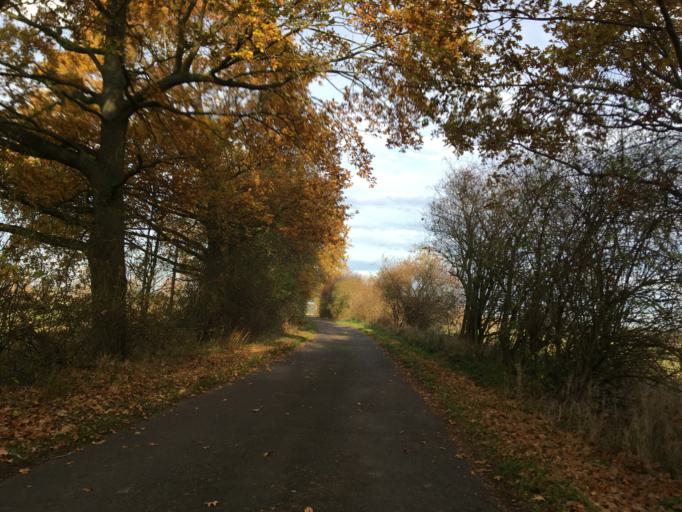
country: DE
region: Brandenburg
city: Luebben
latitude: 51.9759
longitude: 13.8768
